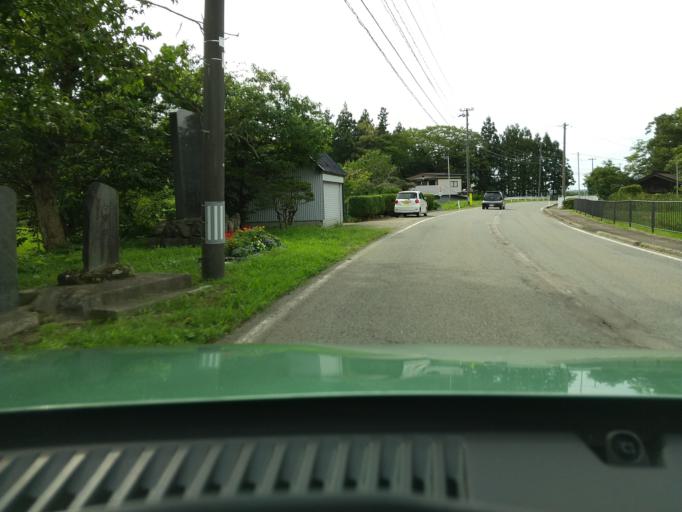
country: JP
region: Akita
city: Akita Shi
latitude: 39.7895
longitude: 140.1140
